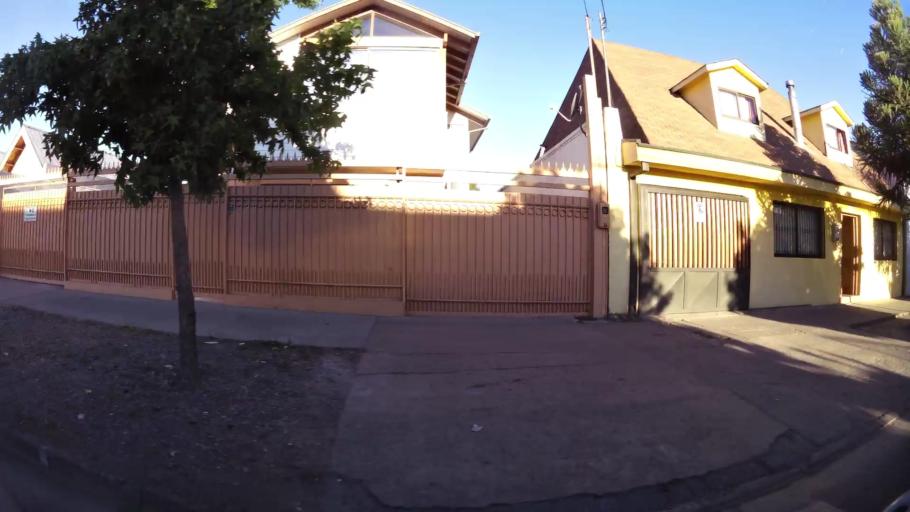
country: CL
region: Maule
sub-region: Provincia de Curico
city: Curico
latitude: -34.9778
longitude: -71.2435
